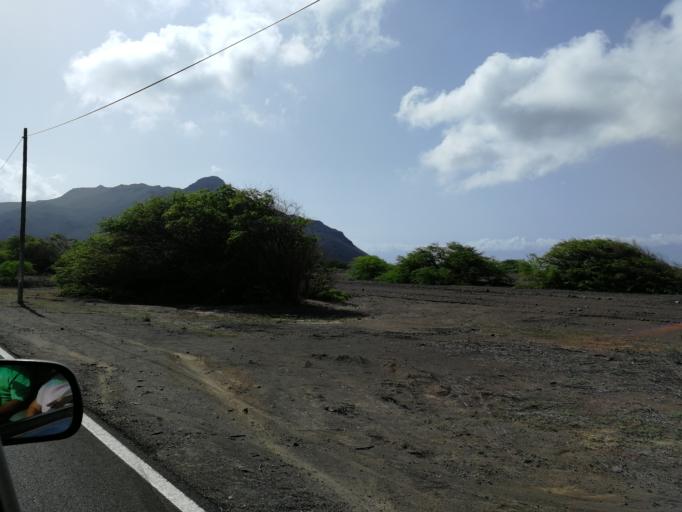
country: CV
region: Sao Vicente
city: Mindelo
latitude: 16.8964
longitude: -24.9290
